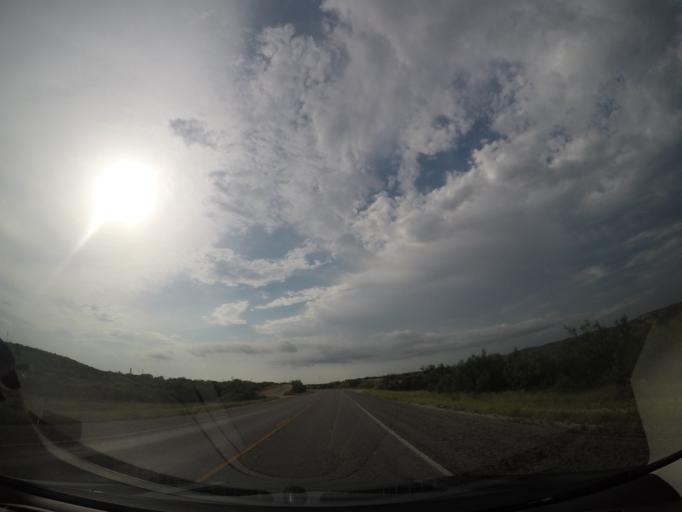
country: US
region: Texas
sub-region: Val Verde County
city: Cienegas Terrace
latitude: 29.8214
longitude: -101.6116
